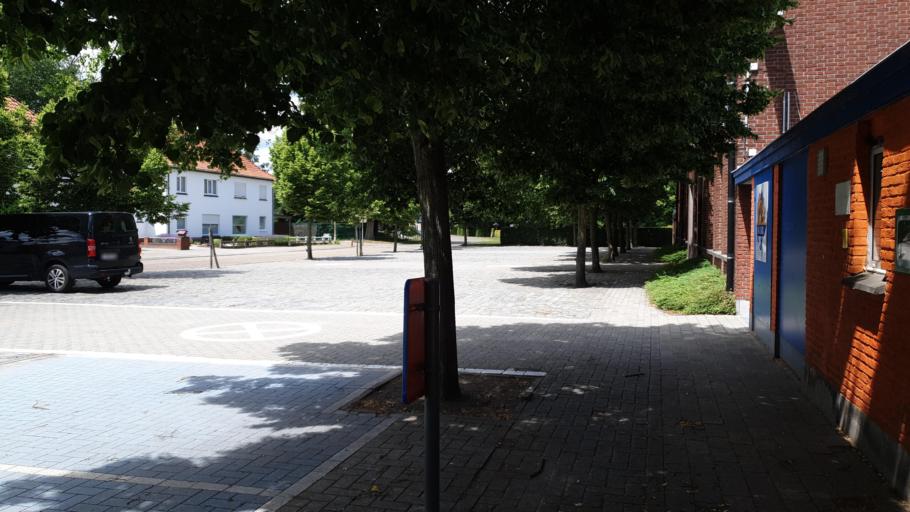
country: BE
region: Flanders
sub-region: Provincie Antwerpen
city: Beerse
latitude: 51.3112
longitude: 4.8460
